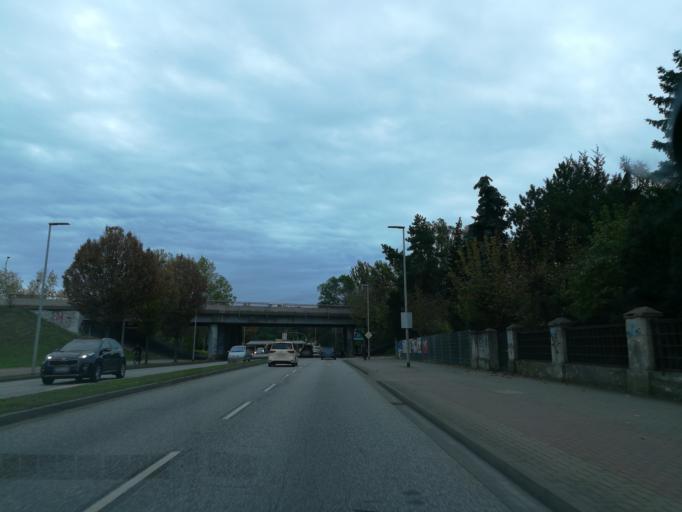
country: DE
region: Saxony-Anhalt
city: Neue Neustadt
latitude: 52.1406
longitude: 11.6279
